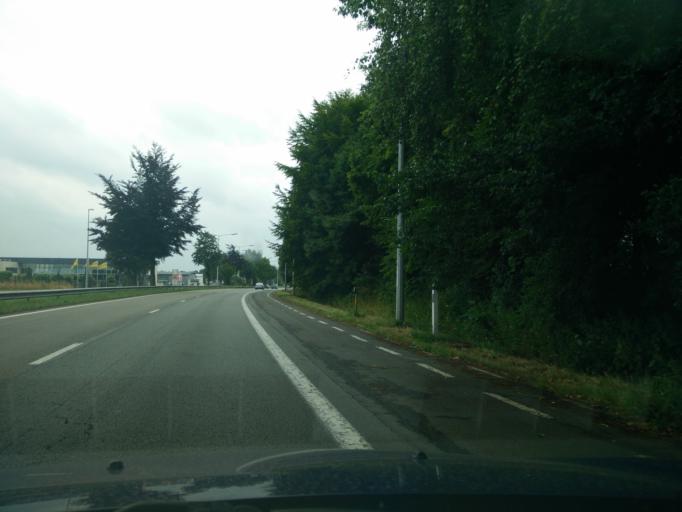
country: BE
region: Flanders
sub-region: Provincie Oost-Vlaanderen
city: Oudenaarde
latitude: 50.8788
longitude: 3.6153
